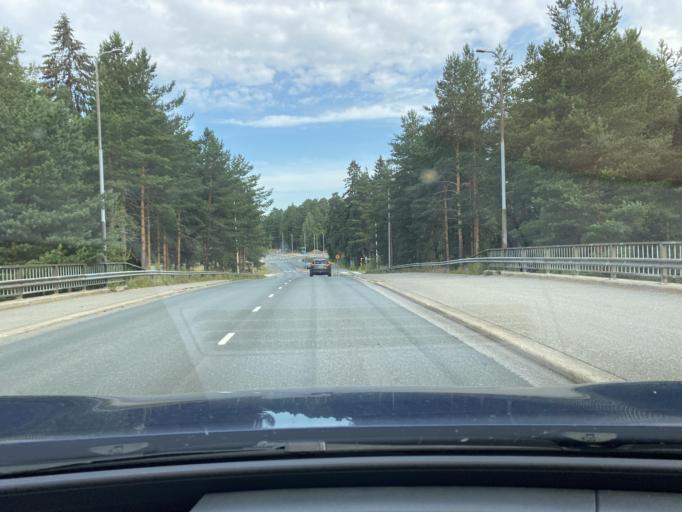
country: FI
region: Pirkanmaa
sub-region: Lounais-Pirkanmaa
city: Vammala
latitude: 61.3508
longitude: 22.8979
